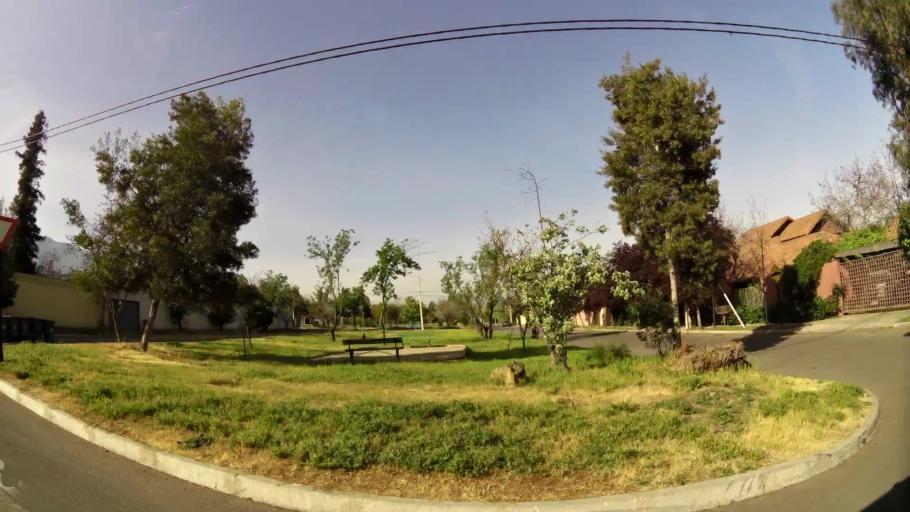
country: CL
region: Santiago Metropolitan
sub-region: Provincia de Santiago
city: Villa Presidente Frei, Nunoa, Santiago, Chile
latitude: -33.4933
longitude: -70.5453
